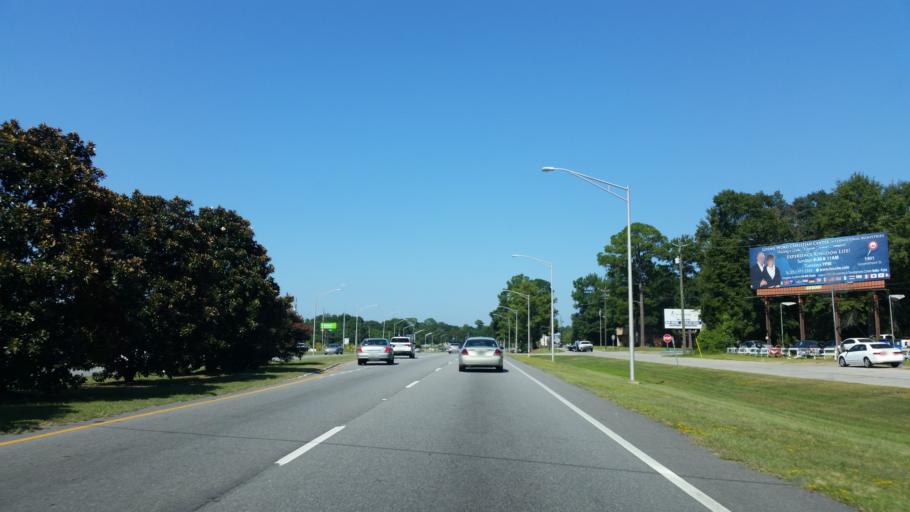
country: US
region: Alabama
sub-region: Mobile County
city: Mobile
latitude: 30.6675
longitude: -88.1044
